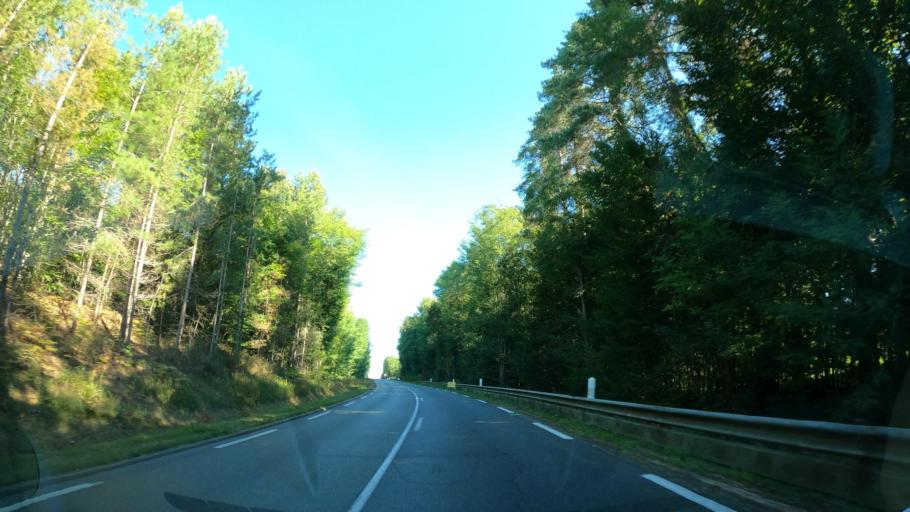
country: FR
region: Aquitaine
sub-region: Departement de la Dordogne
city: Notre-Dame-de-Sanilhac
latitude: 45.0896
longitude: 0.6913
